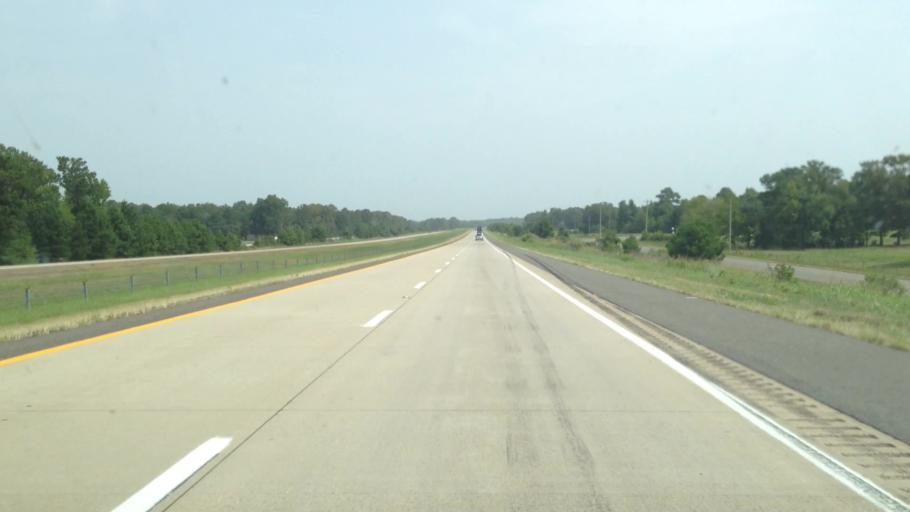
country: US
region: Texas
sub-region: Cass County
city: Queen City
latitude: 33.1829
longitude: -93.8776
